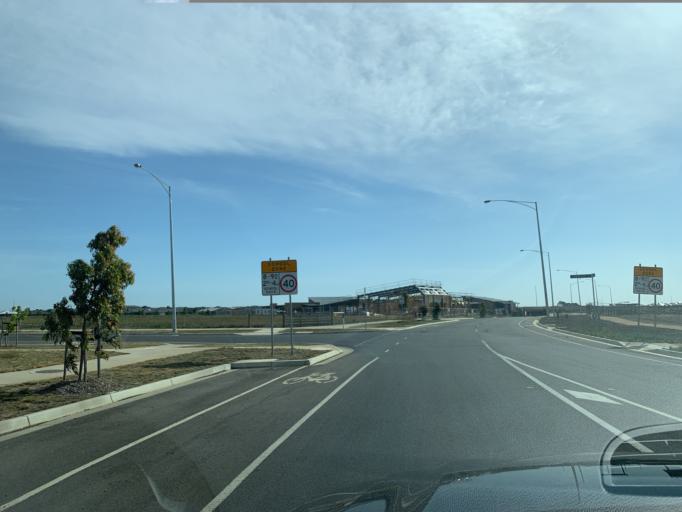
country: AU
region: Victoria
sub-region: Ballarat North
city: Newington
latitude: -37.5452
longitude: 143.7821
